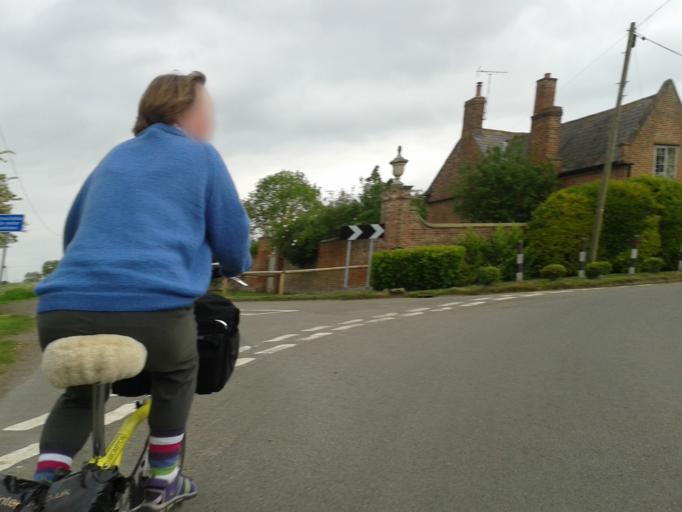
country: GB
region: England
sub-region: Leicestershire
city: Countesthorpe
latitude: 52.5224
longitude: -1.1521
